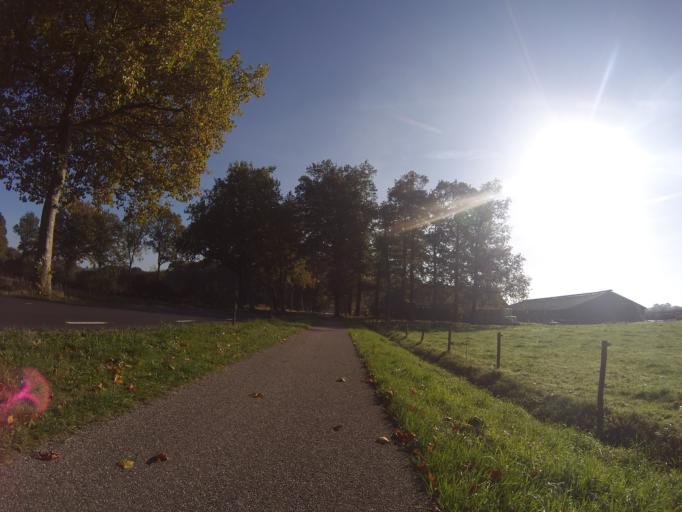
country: NL
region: Gelderland
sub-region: Gemeente Barneveld
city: Terschuur
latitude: 52.1816
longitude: 5.5378
